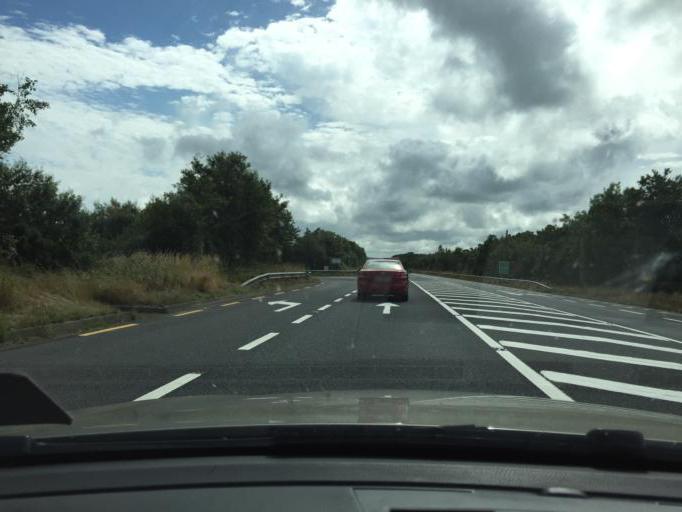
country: IE
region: Munster
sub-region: Waterford
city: Portlaw
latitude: 52.2110
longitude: -7.3944
